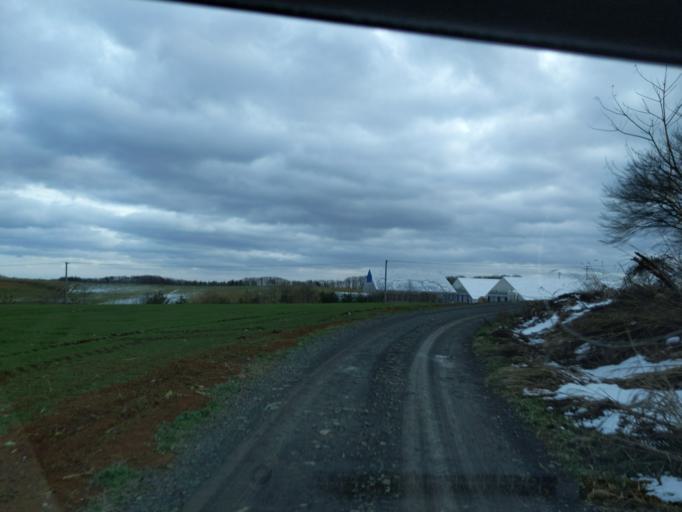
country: JP
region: Iwate
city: Ichinoseki
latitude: 38.9782
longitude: 141.0146
